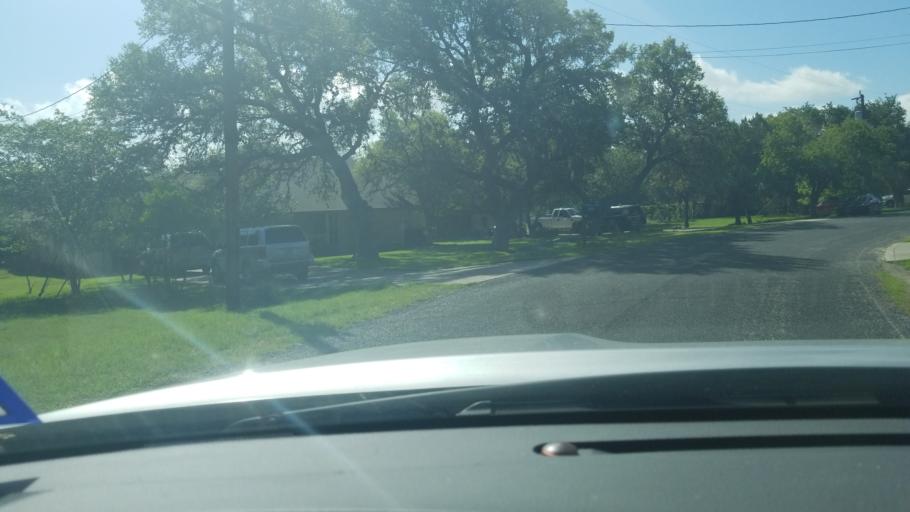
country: US
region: Texas
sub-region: Bexar County
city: Timberwood Park
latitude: 29.7065
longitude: -98.4855
